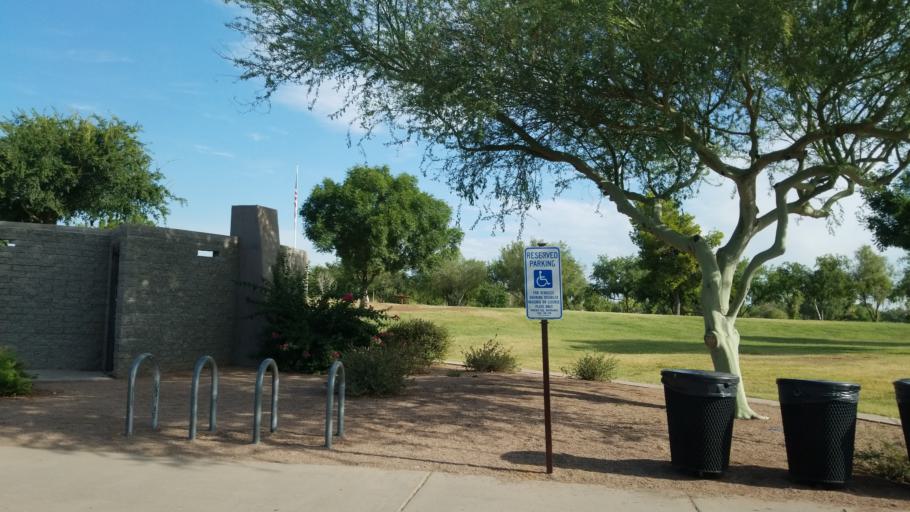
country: US
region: Arizona
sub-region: Maricopa County
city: Phoenix
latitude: 33.4990
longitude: -112.0688
